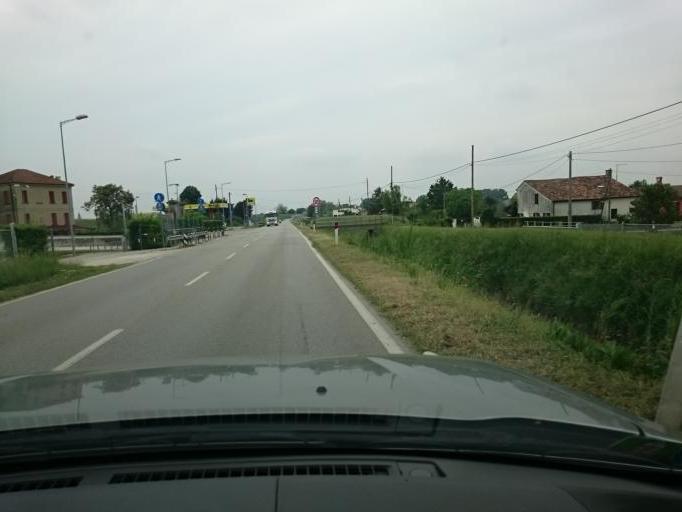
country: IT
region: Veneto
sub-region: Provincia di Padova
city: Bovolenta
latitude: 45.2765
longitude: 11.9315
